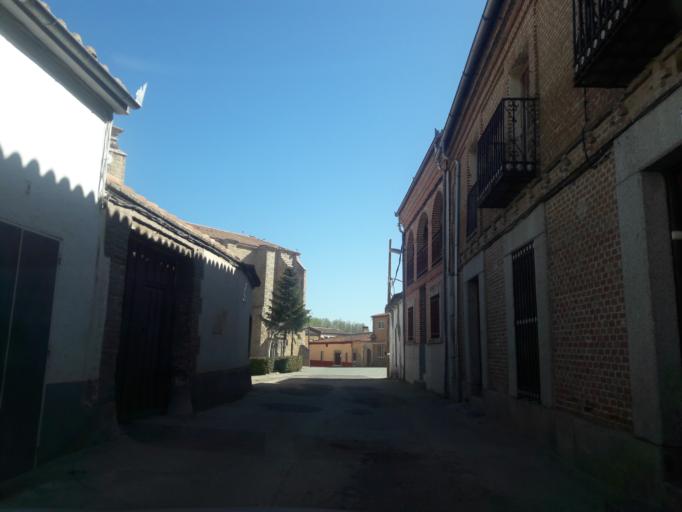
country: ES
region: Castille and Leon
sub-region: Provincia de Salamanca
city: Salmoral
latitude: 40.8010
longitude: -5.2201
